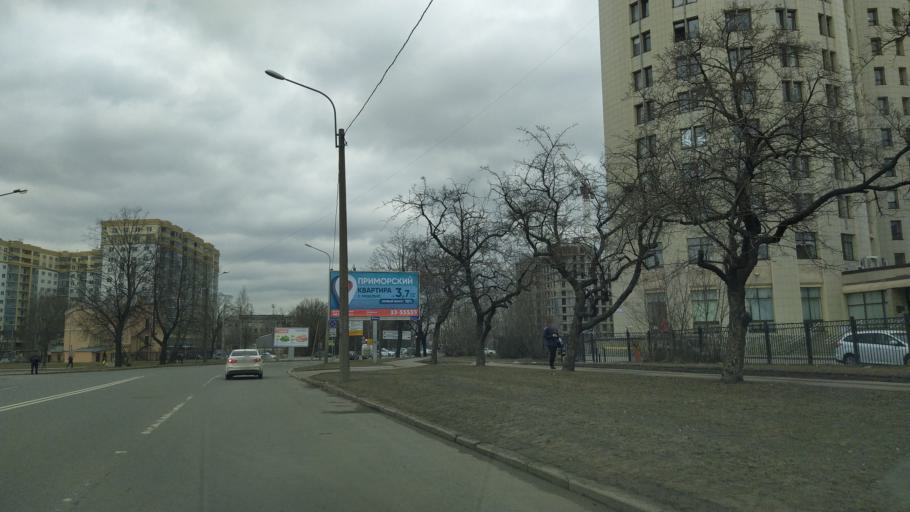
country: RU
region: St.-Petersburg
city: Centralniy
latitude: 59.9321
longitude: 30.4159
